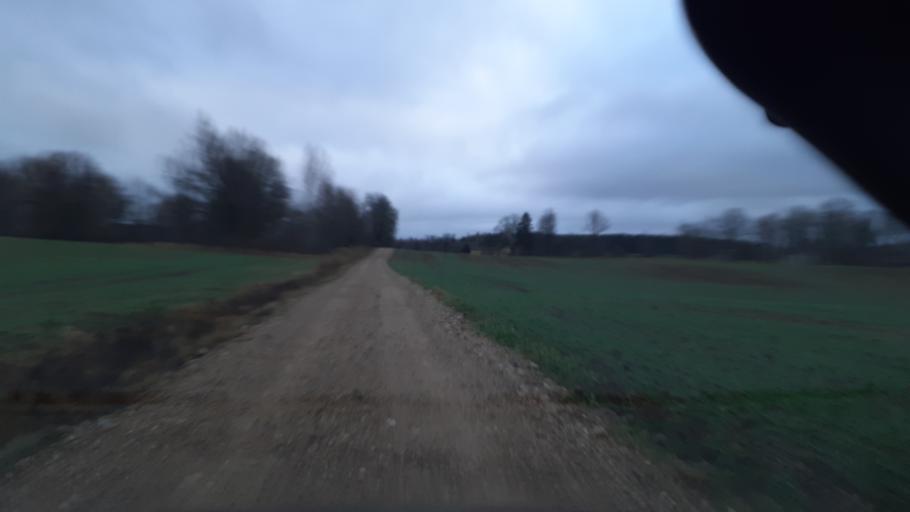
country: LV
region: Alsunga
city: Alsunga
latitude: 56.8769
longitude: 21.6855
